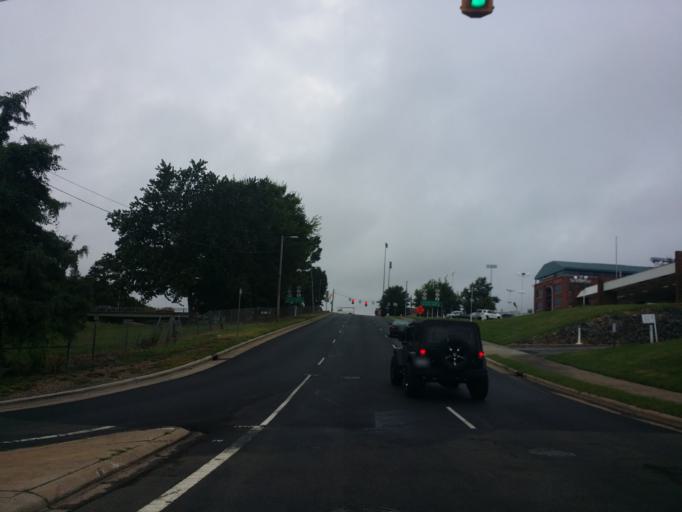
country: US
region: North Carolina
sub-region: Durham County
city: Durham
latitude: 35.9899
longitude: -78.9012
